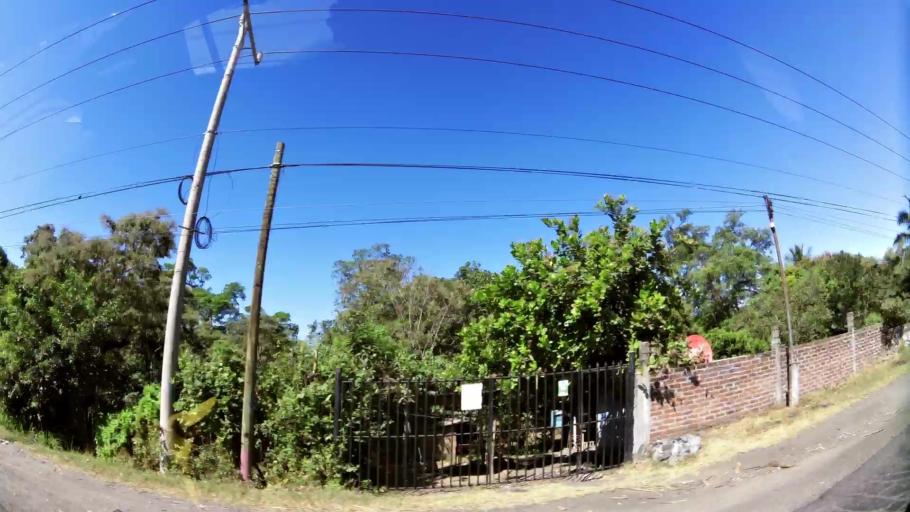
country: SV
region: La Libertad
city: San Juan Opico
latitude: 13.8054
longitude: -89.3587
